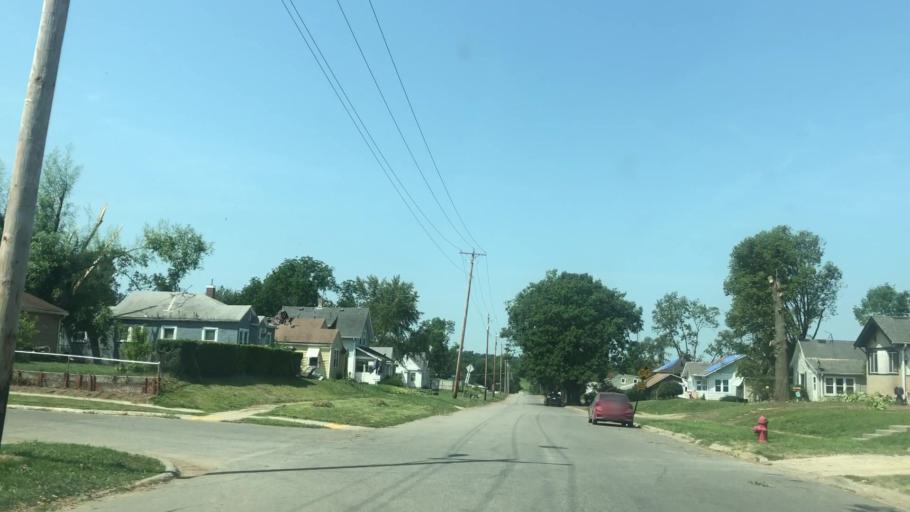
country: US
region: Iowa
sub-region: Marshall County
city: Marshalltown
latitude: 42.0527
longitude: -92.9438
